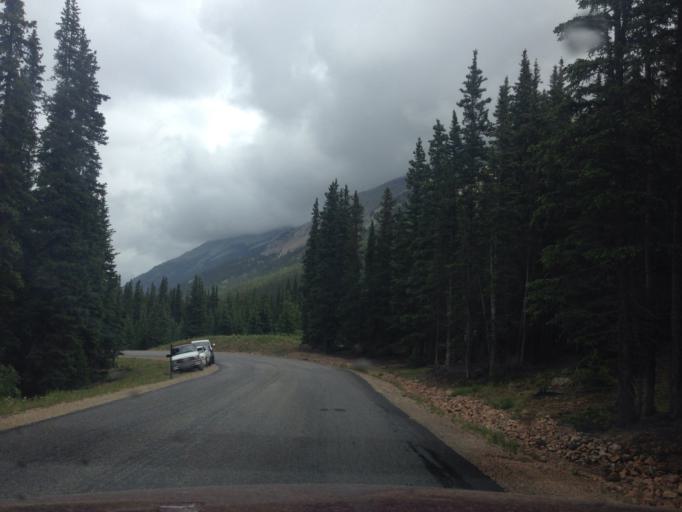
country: US
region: Colorado
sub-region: Clear Creek County
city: Georgetown
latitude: 39.6100
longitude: -105.7176
